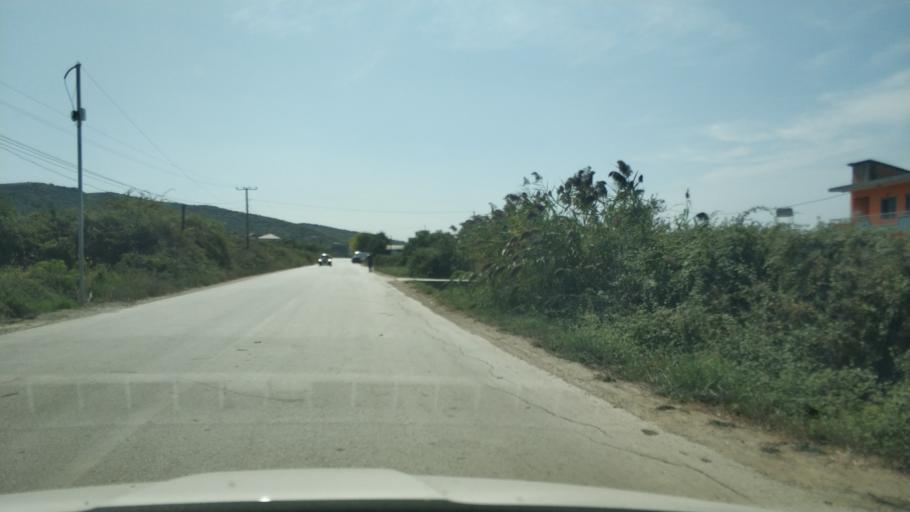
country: AL
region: Fier
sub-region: Rrethi i Lushnjes
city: Grabjan
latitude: 40.9468
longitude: 19.5369
